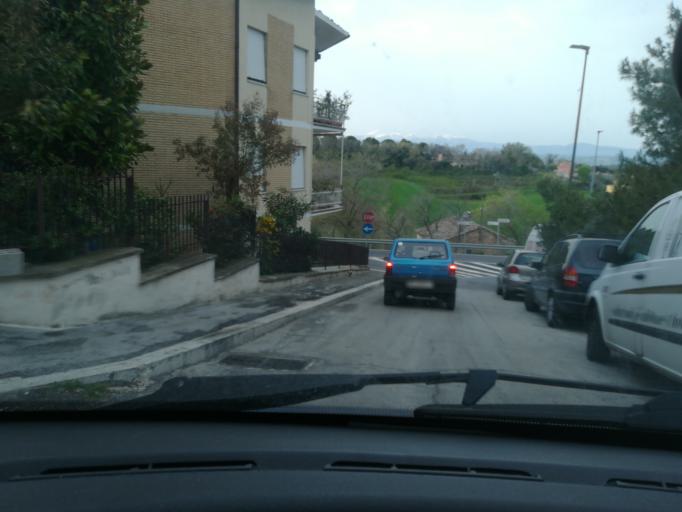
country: IT
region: The Marches
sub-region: Provincia di Macerata
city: Macerata
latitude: 43.2929
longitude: 13.4521
